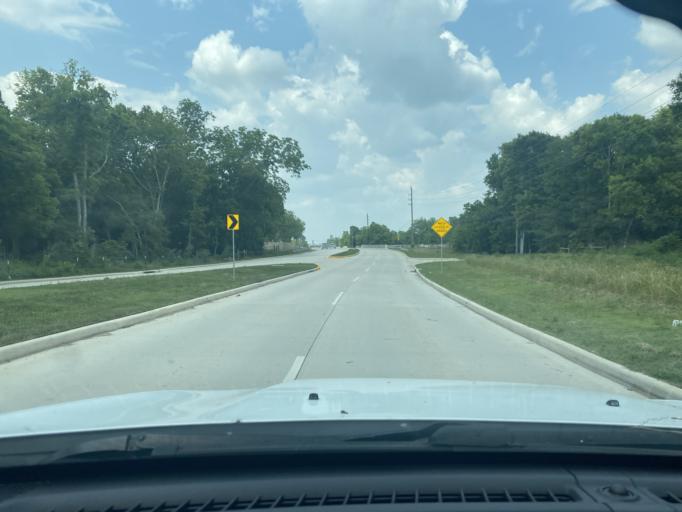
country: US
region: Texas
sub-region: Fort Bend County
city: Greatwood
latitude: 29.5443
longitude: -95.7231
